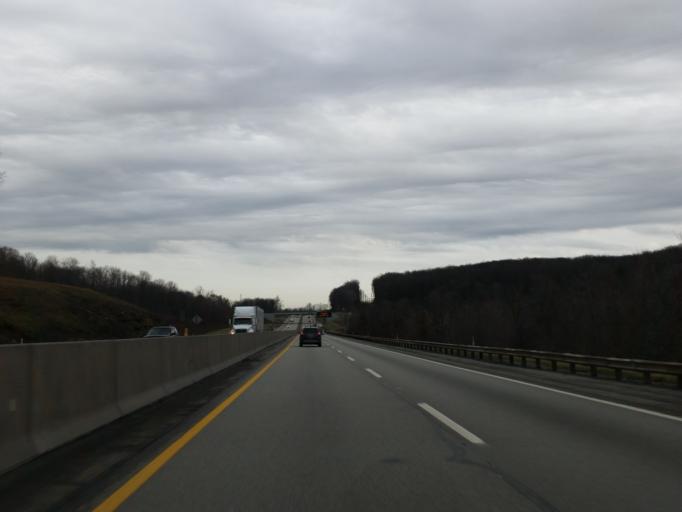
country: US
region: Pennsylvania
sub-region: Somerset County
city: Somerset
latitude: 40.0676
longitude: -79.1536
